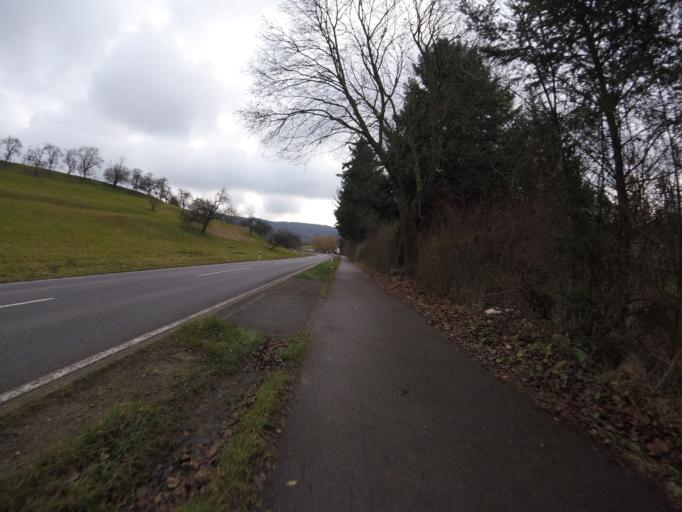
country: DE
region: Baden-Wuerttemberg
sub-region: Regierungsbezirk Stuttgart
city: Allmersbach im Tal
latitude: 48.9133
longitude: 9.4839
